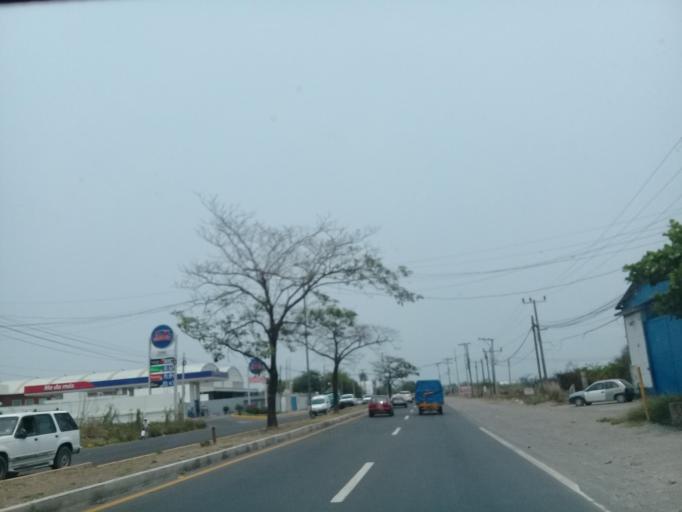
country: MX
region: Veracruz
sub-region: Veracruz
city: Las Amapolas
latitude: 19.1565
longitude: -96.1917
